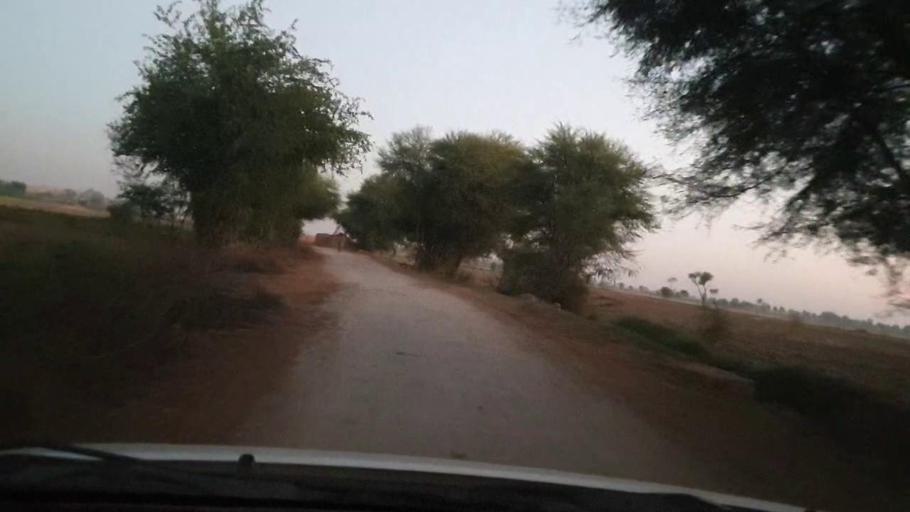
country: PK
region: Sindh
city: Khairpur Nathan Shah
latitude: 27.1338
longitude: 67.7224
